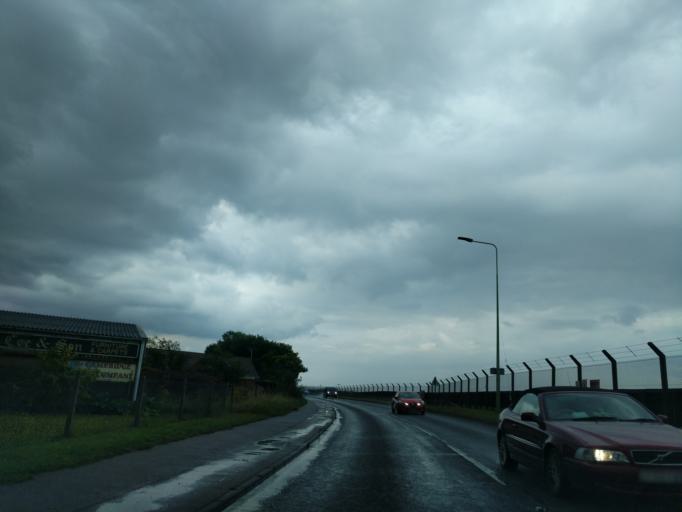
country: GB
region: England
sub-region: Suffolk
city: Lakenheath
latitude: 52.3652
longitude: 0.4904
